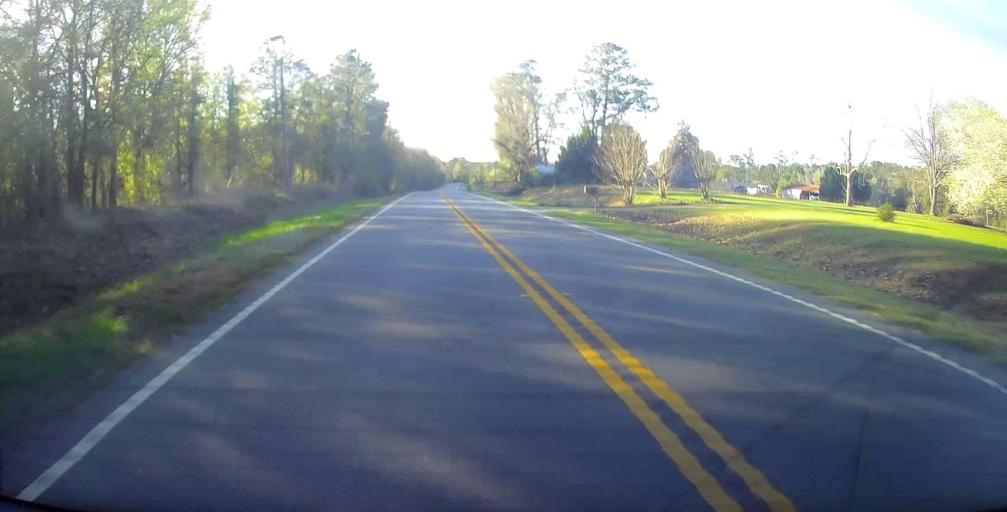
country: US
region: Georgia
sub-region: Pulaski County
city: Hawkinsville
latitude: 32.2667
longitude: -83.4305
